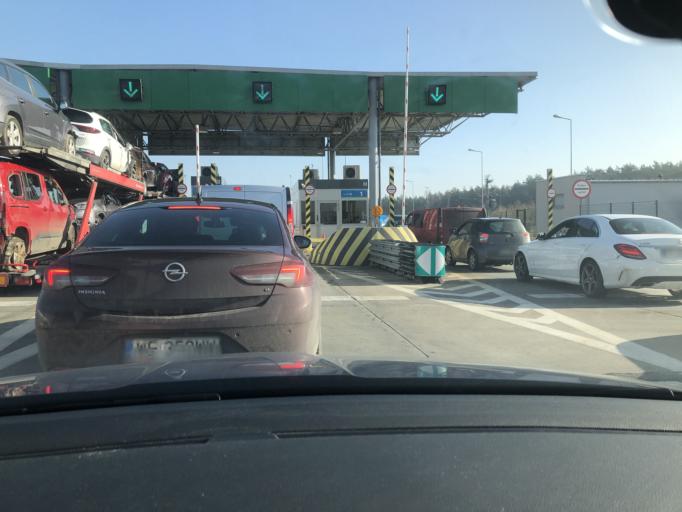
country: PL
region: Greater Poland Voivodeship
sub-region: Powiat poznanski
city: Buk
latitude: 52.3782
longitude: 16.5683
